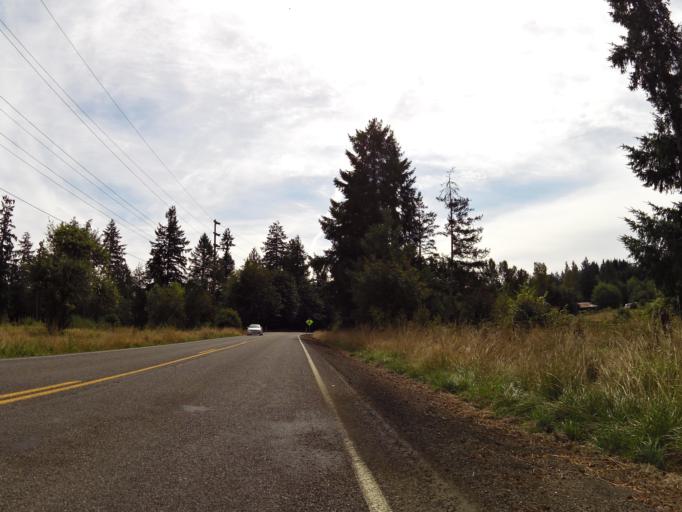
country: US
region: Washington
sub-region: Lewis County
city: Winlock
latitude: 46.4344
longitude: -122.9702
